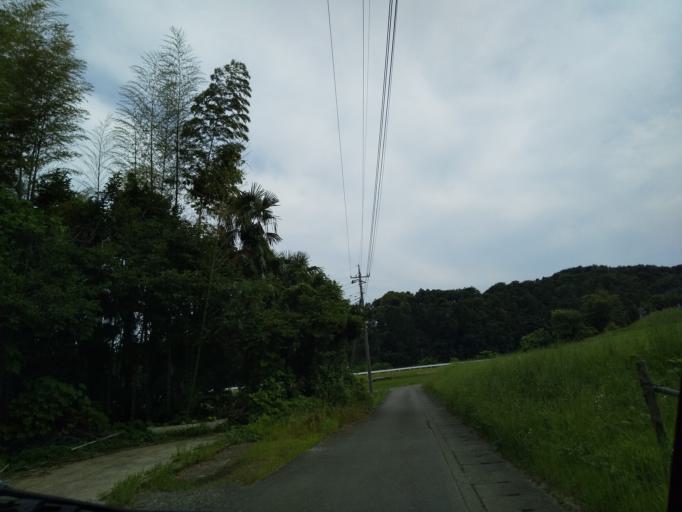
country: JP
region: Kanagawa
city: Atsugi
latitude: 35.4839
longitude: 139.3265
